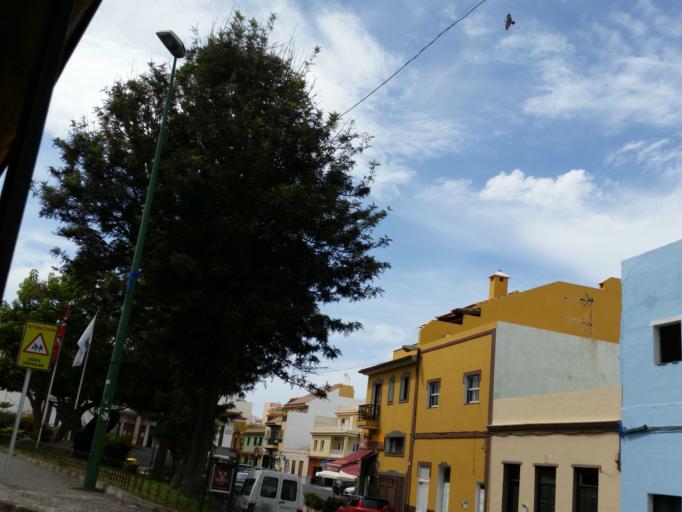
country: ES
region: Canary Islands
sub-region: Provincia de Santa Cruz de Tenerife
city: Puerto de la Cruz
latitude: 28.4102
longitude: -16.5646
